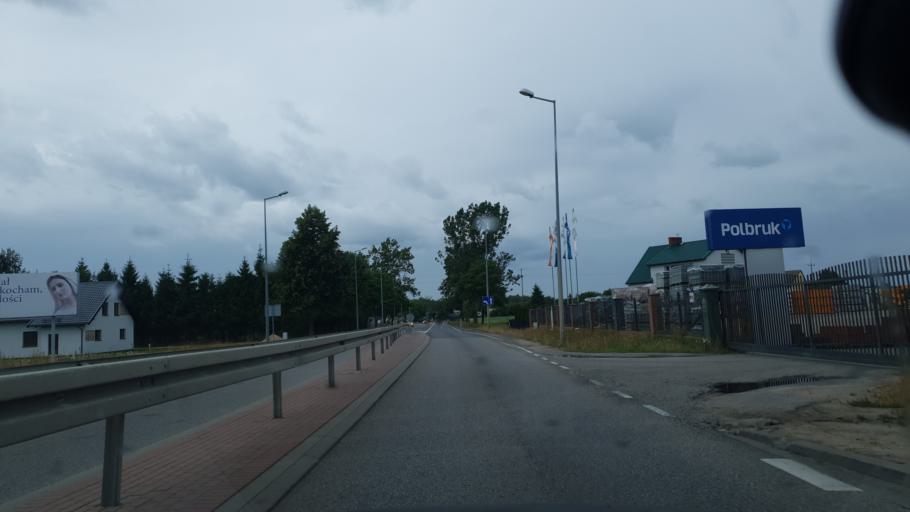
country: PL
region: Pomeranian Voivodeship
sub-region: Powiat kartuski
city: Banino
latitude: 54.3897
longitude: 18.3595
